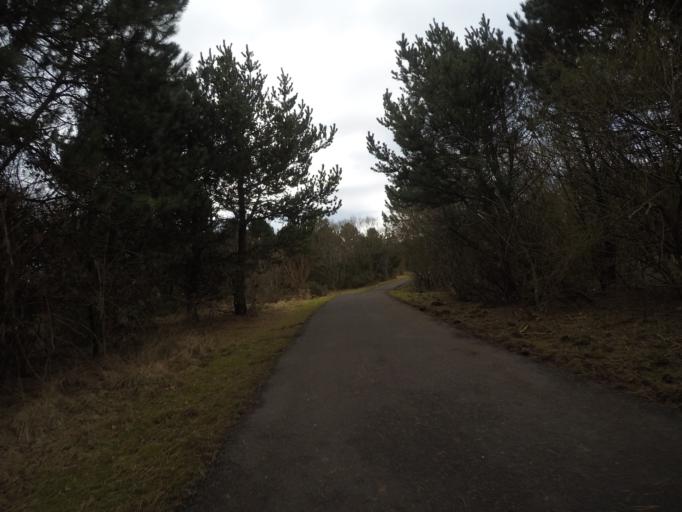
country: GB
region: Scotland
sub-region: North Ayrshire
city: Irvine
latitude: 55.5971
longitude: -4.6752
